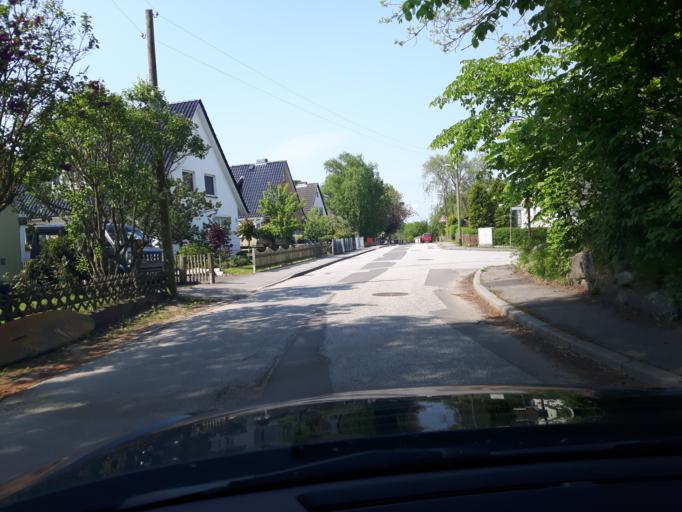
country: DE
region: Schleswig-Holstein
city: Travemuende
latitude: 53.9396
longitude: 10.8391
